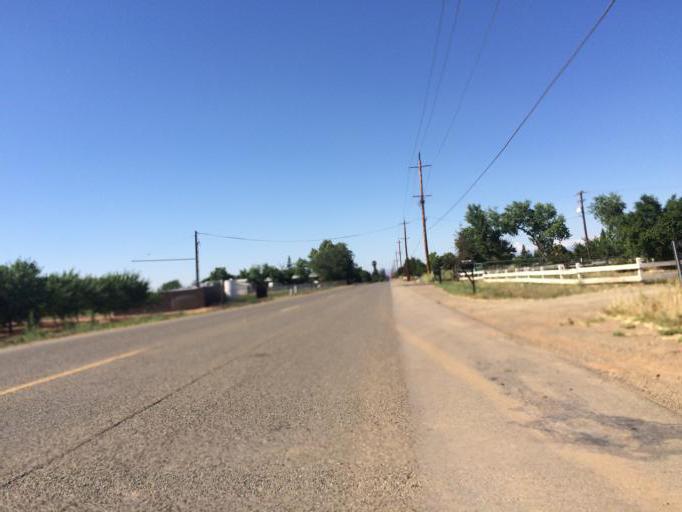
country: US
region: California
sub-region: Fresno County
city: Tarpey Village
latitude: 36.7824
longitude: -119.6102
